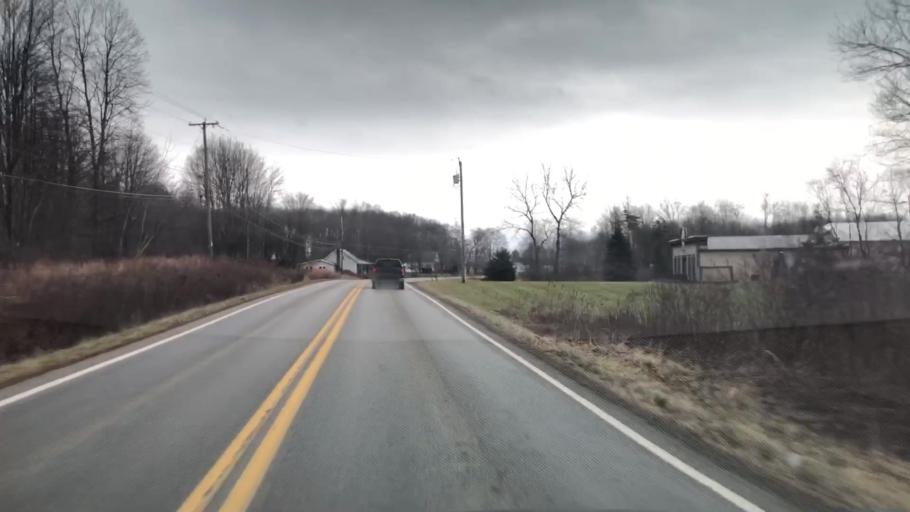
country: US
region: Pennsylvania
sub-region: Mercer County
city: Grove City
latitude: 41.1370
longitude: -80.1373
